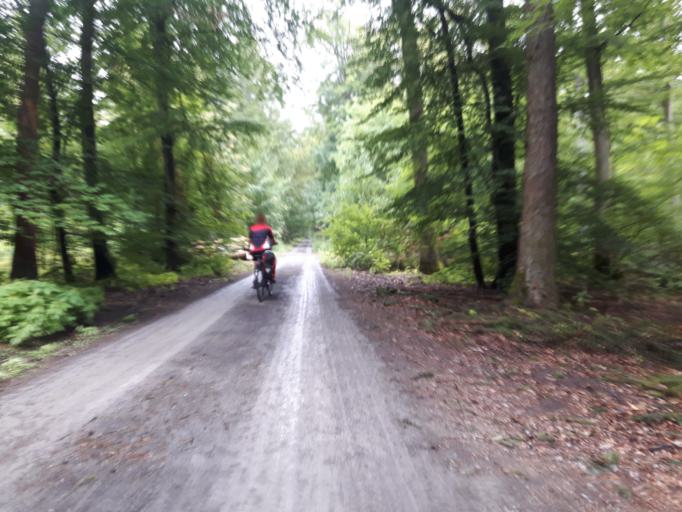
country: DE
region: Baden-Wuerttemberg
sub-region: Regierungsbezirk Stuttgart
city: Eppingen
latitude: 49.1189
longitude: 8.9410
